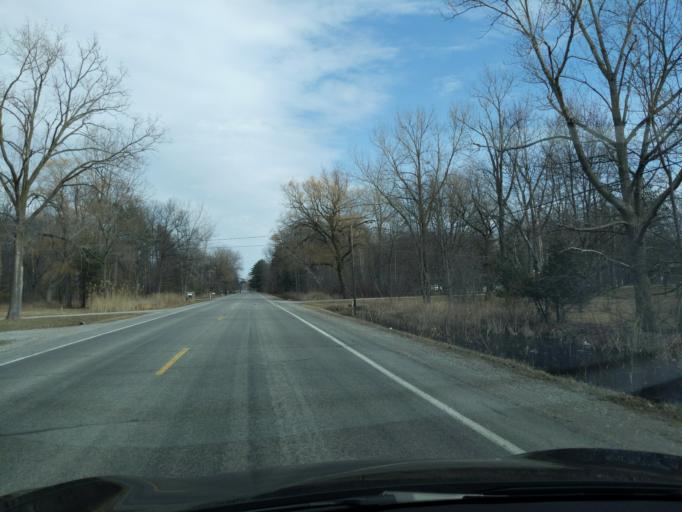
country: US
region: Michigan
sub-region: Bay County
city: Bay City
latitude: 43.6675
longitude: -83.9278
